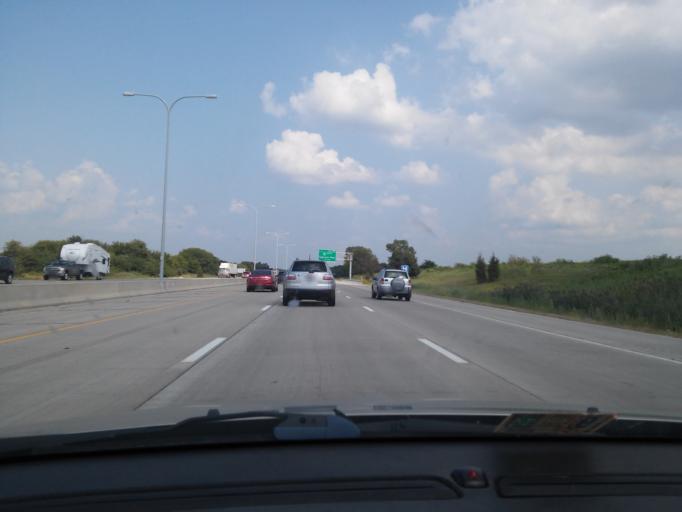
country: US
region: Illinois
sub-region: McLean County
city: Normal
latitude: 40.5387
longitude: -88.9705
